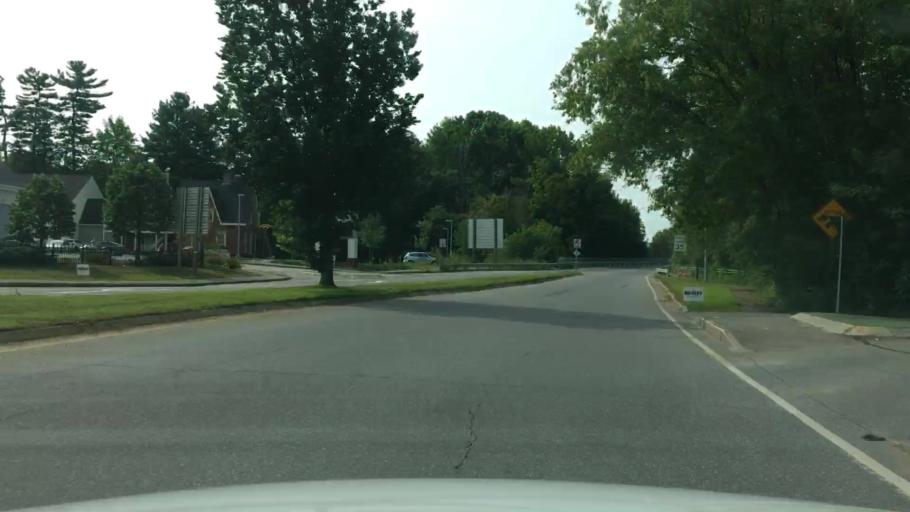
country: US
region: Maine
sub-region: Kennebec County
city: Augusta
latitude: 44.3160
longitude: -69.7684
